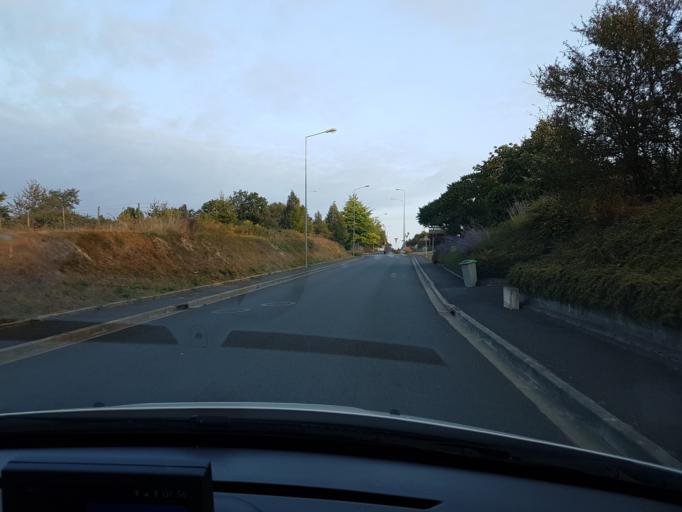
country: FR
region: Centre
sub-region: Departement d'Indre-et-Loire
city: Saint-Avertin
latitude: 47.3610
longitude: 0.7546
